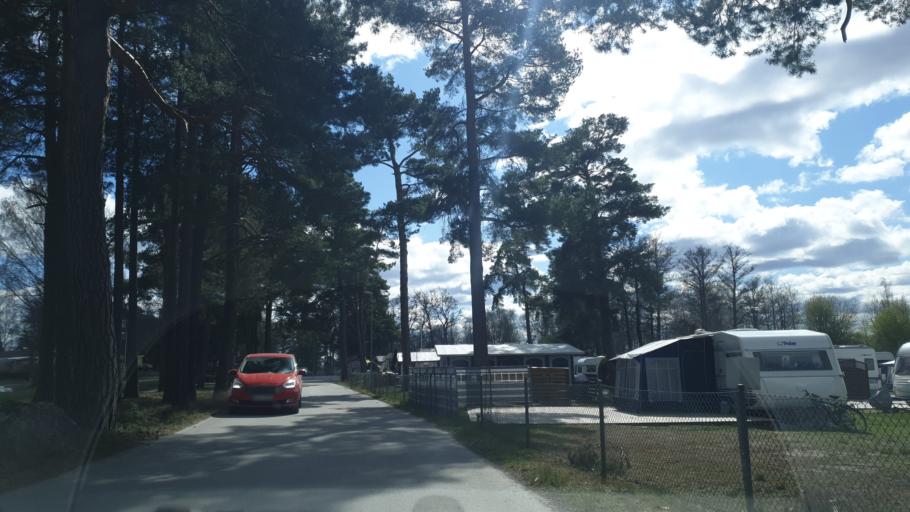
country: SE
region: Vaestmanland
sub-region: Kungsors Kommun
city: Kungsoer
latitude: 59.4744
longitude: 16.0645
